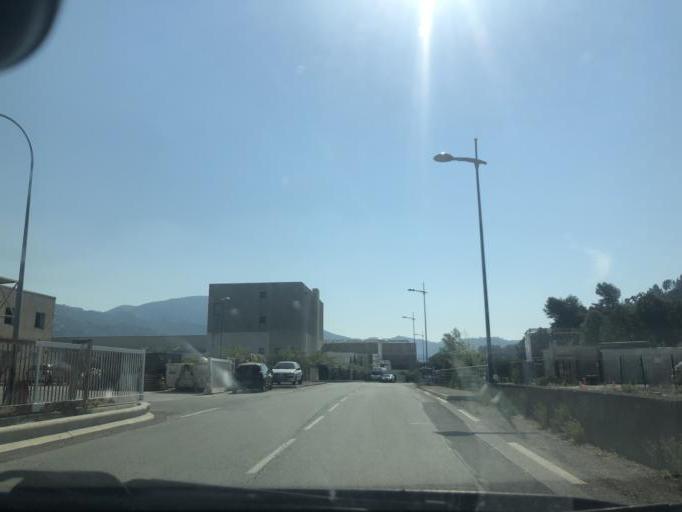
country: FR
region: Provence-Alpes-Cote d'Azur
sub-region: Departement des Alpes-Maritimes
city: Carros
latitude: 43.7991
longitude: 7.1959
